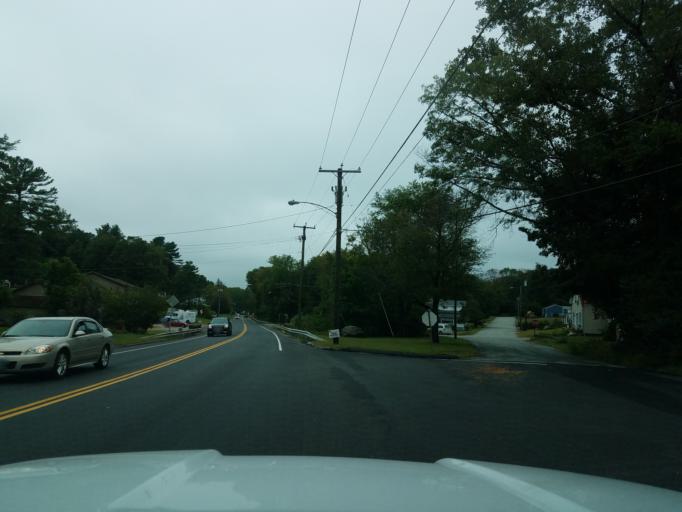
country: US
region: Connecticut
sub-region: Windham County
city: Putnam
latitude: 41.9247
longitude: -71.8934
